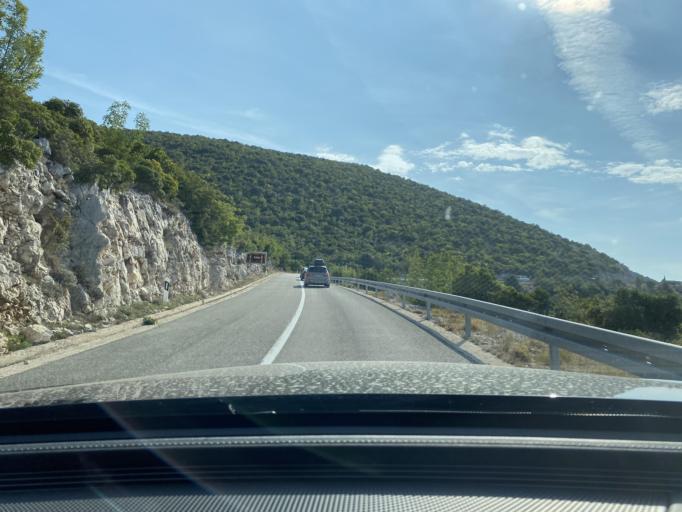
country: HR
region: Dubrovacko-Neretvanska
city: Orebic
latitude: 42.9695
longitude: 17.2508
